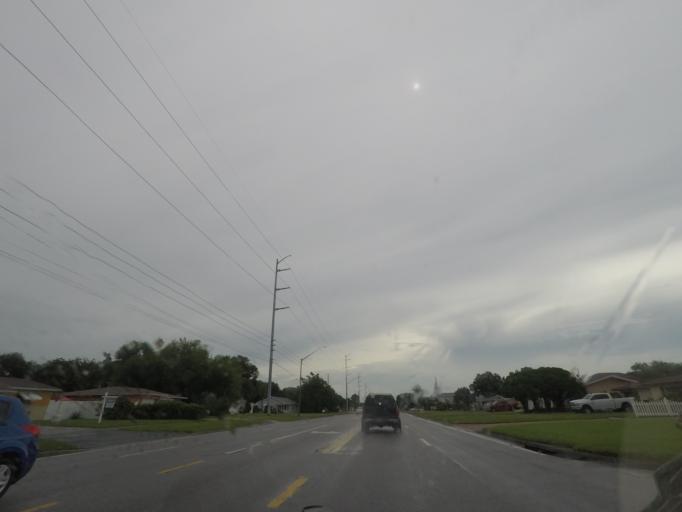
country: US
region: Florida
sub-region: Pinellas County
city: Kenneth City
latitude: 27.8064
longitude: -82.7202
